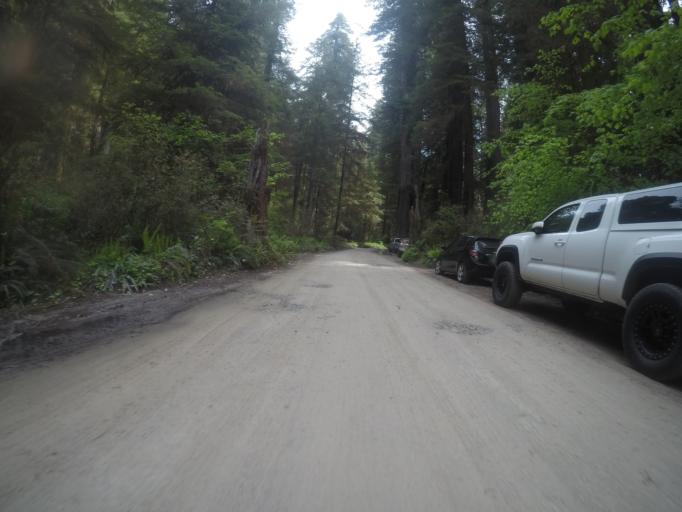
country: US
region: California
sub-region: Del Norte County
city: Bertsch-Oceanview
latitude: 41.7689
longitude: -124.1094
